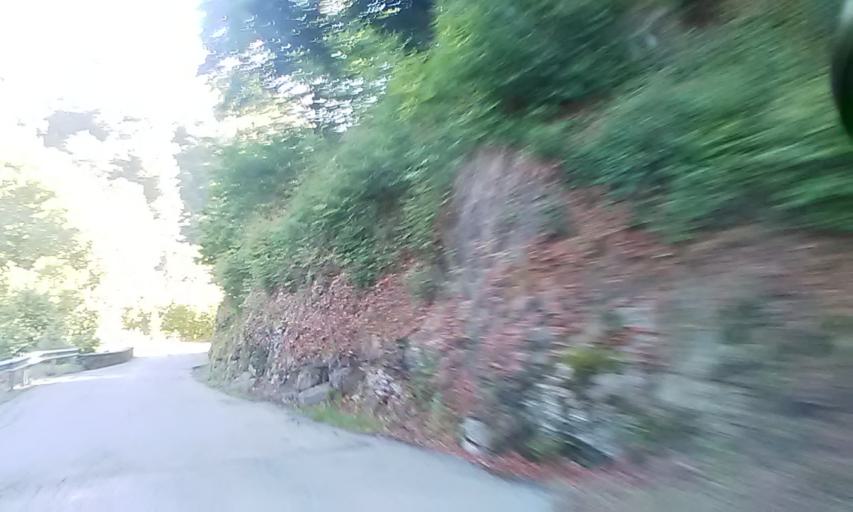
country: IT
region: Piedmont
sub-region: Provincia di Vercelli
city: Civiasco
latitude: 45.8422
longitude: 8.2814
